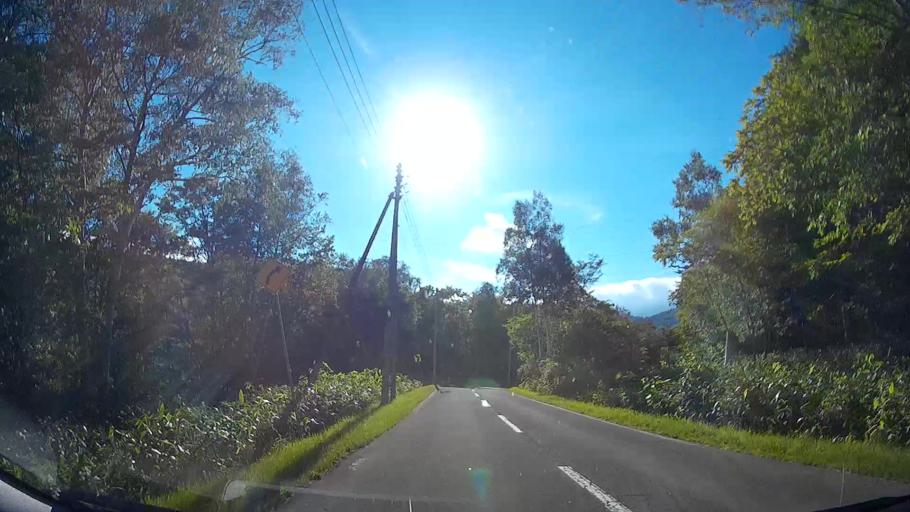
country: JP
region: Hokkaido
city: Sapporo
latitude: 42.9842
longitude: 141.1251
